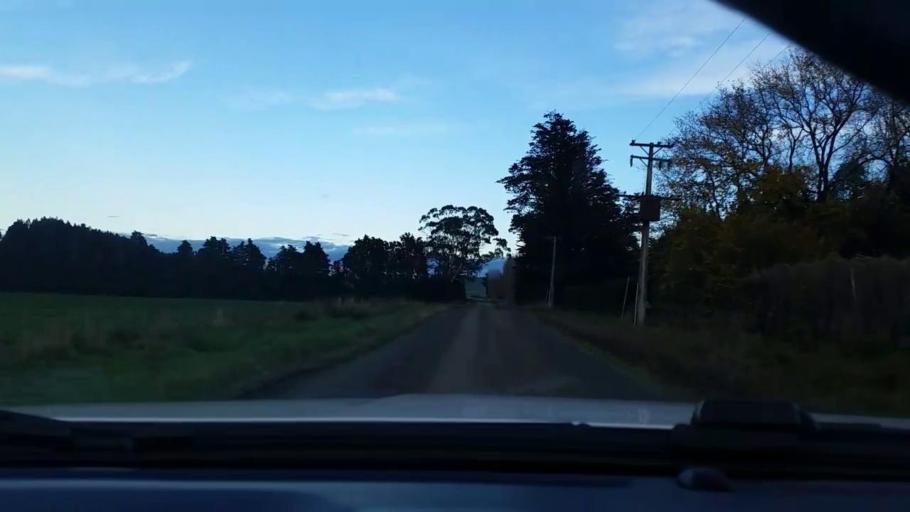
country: NZ
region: Southland
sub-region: Southland District
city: Winton
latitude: -46.1039
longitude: 168.4599
